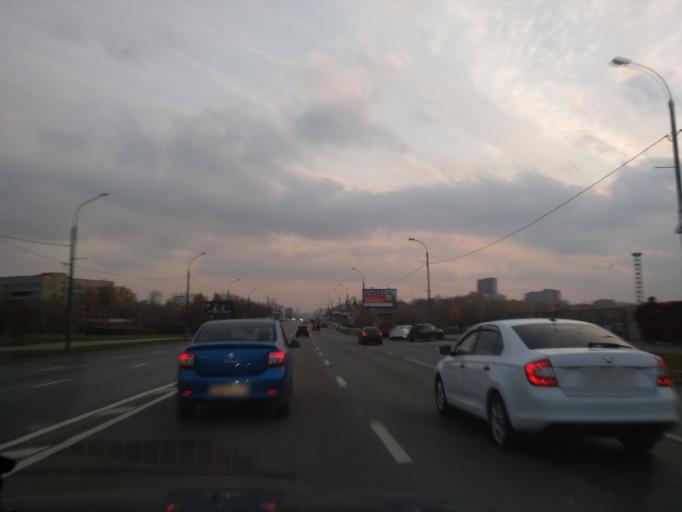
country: RU
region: Moscow
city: Vatutino
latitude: 55.8835
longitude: 37.6717
